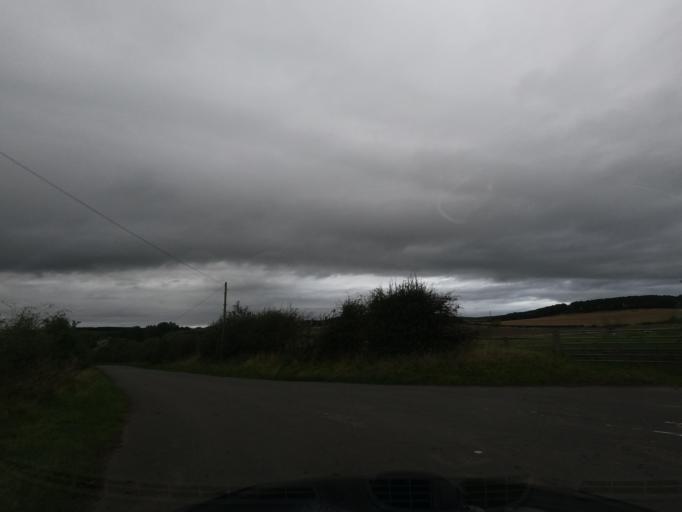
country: GB
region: England
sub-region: Northumberland
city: Ford
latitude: 55.6119
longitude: -2.0691
